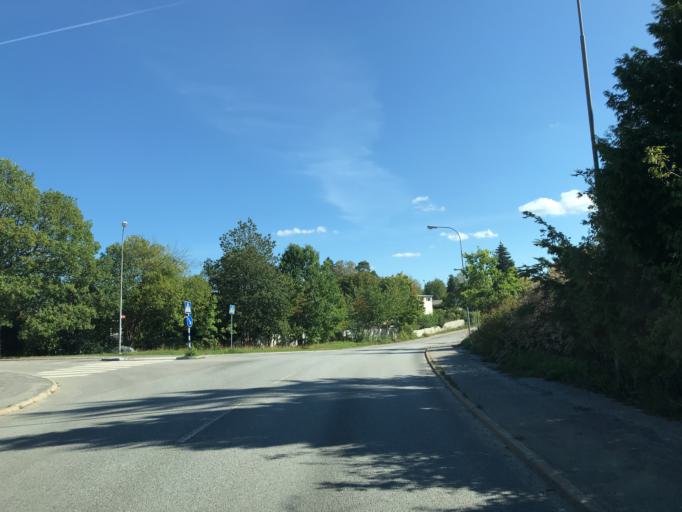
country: SE
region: Stockholm
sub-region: Sollentuna Kommun
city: Sollentuna
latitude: 59.4213
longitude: 17.9488
